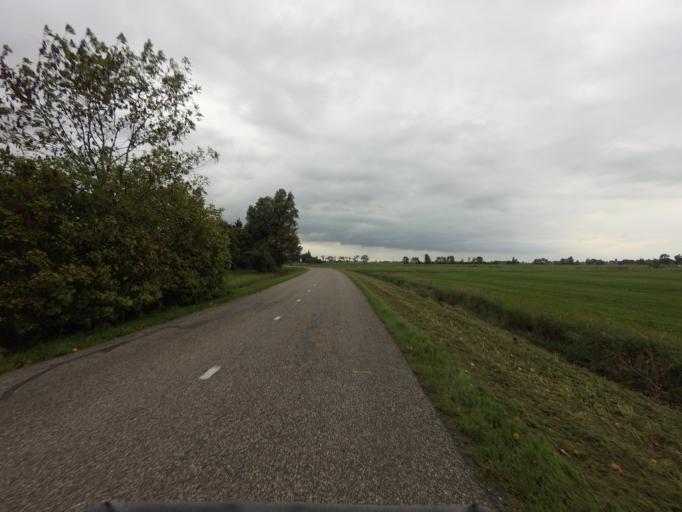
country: NL
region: Friesland
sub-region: Sudwest Fryslan
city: IJlst
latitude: 53.0231
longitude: 5.5976
